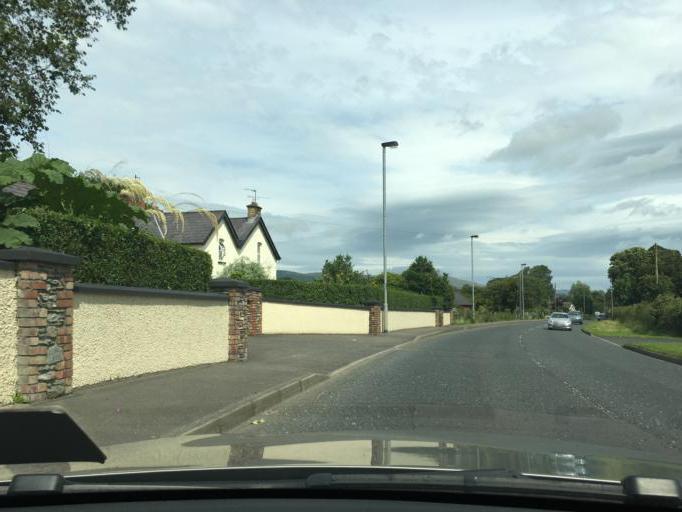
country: IE
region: Ulster
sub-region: County Donegal
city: Muff
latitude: 55.0617
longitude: -7.2716
